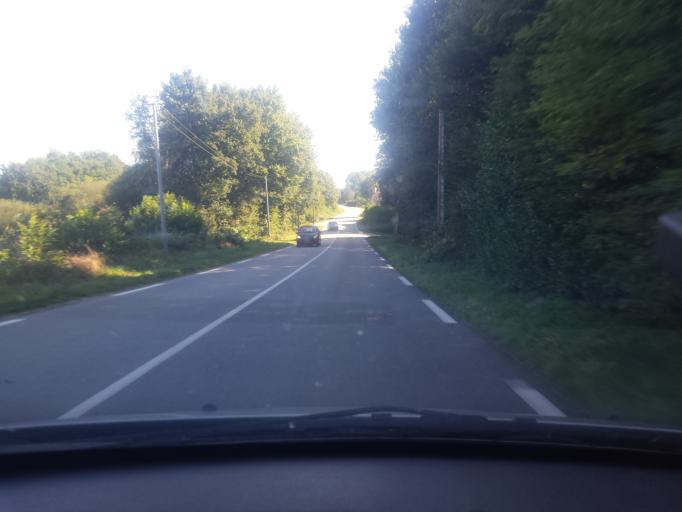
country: FR
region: Brittany
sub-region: Departement du Morbihan
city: Saint-Thuriau
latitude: 48.0411
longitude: -2.9244
